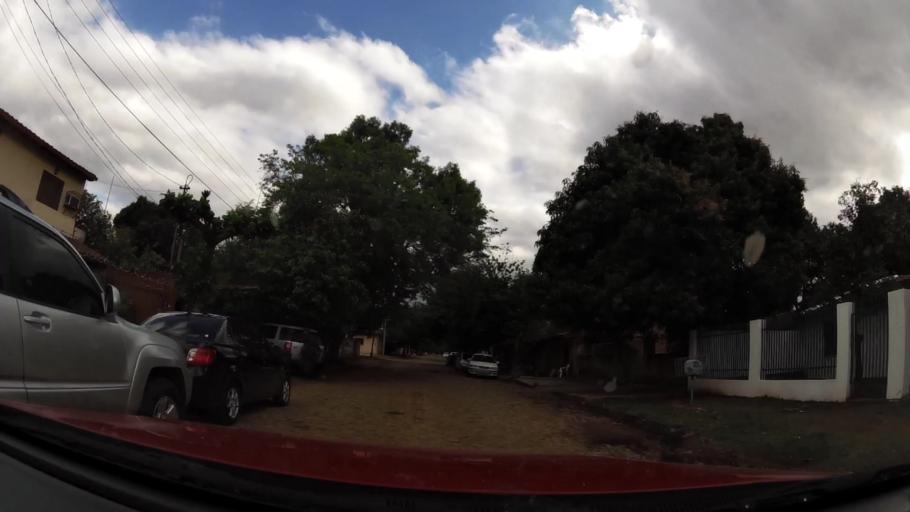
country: PY
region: Central
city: San Lorenzo
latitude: -25.2721
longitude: -57.5049
